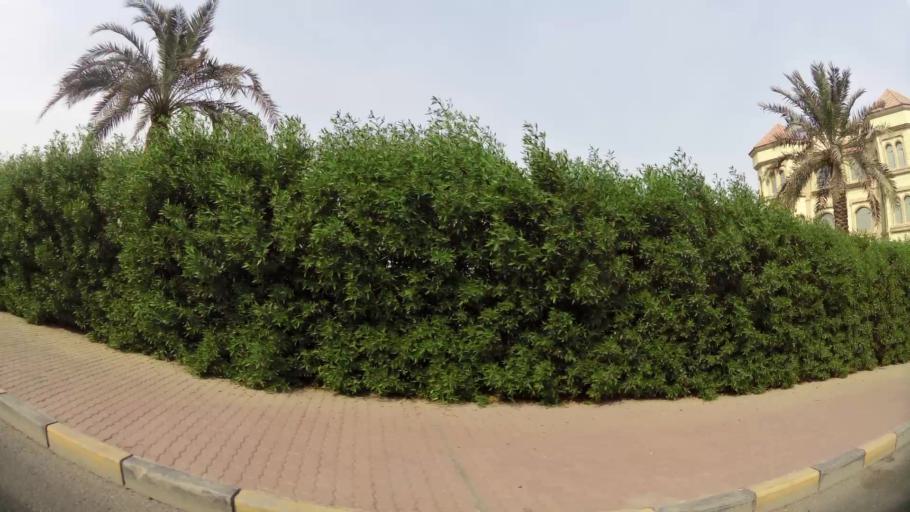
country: KW
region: Al Farwaniyah
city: Al Farwaniyah
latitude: 29.2688
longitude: 47.9362
